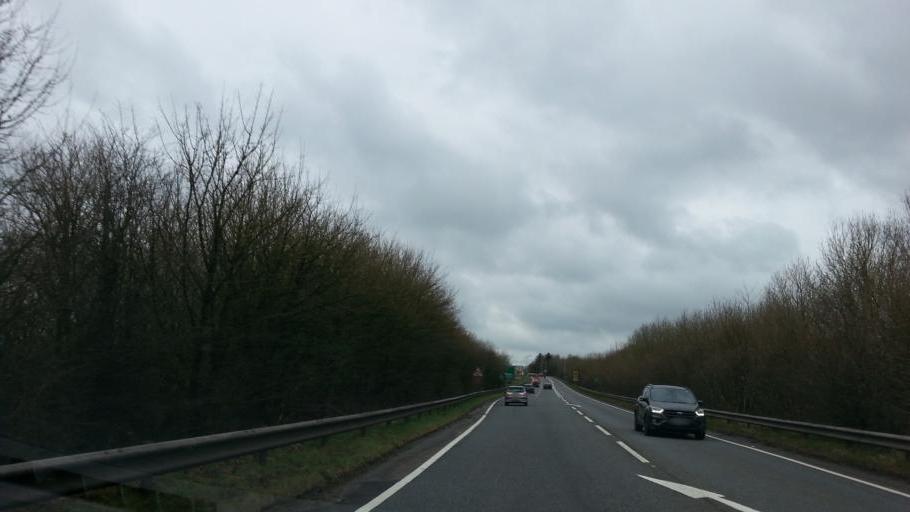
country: GB
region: England
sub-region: Devon
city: South Molton
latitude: 51.0364
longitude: -3.8503
